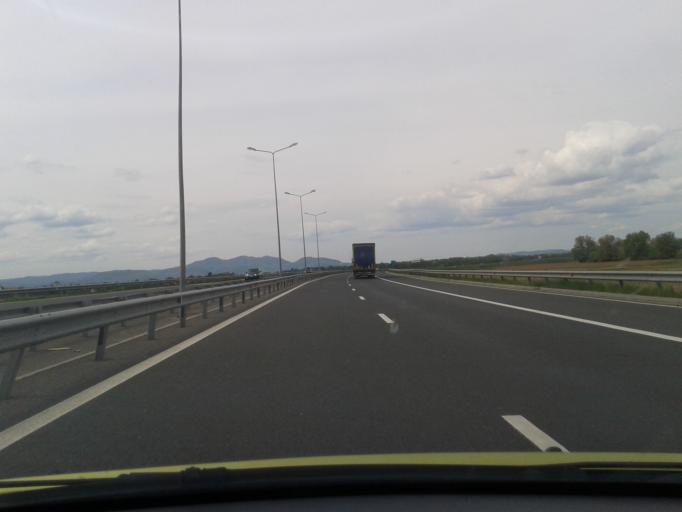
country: RO
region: Hunedoara
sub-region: Comuna Rapoltu Mare
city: Rapoltu Mare
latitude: 45.8500
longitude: 23.0445
